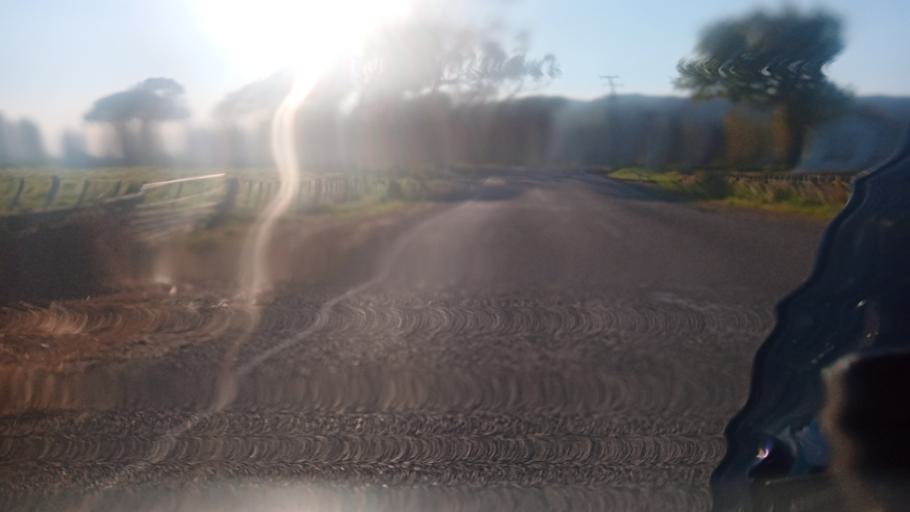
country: NZ
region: Hawke's Bay
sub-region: Wairoa District
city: Wairoa
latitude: -39.0468
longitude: 177.7566
